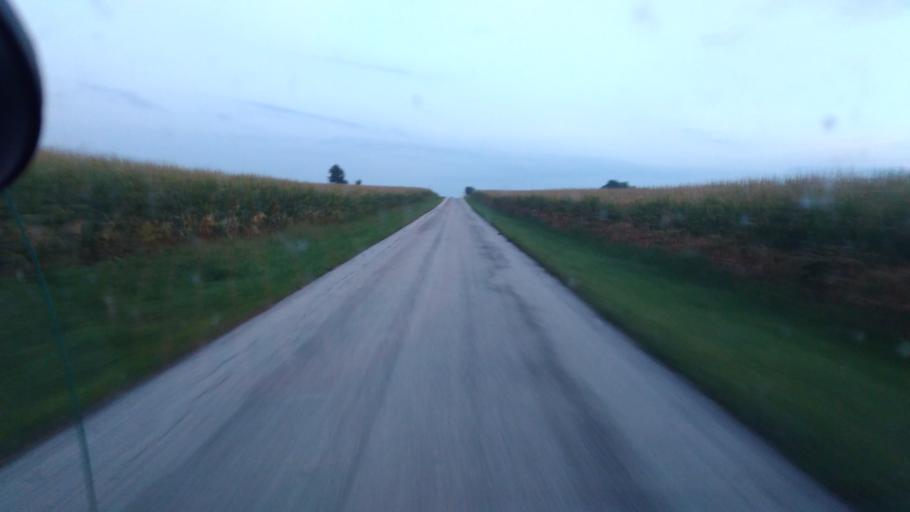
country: US
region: Ohio
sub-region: Hardin County
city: Kenton
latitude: 40.6485
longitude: -83.4583
